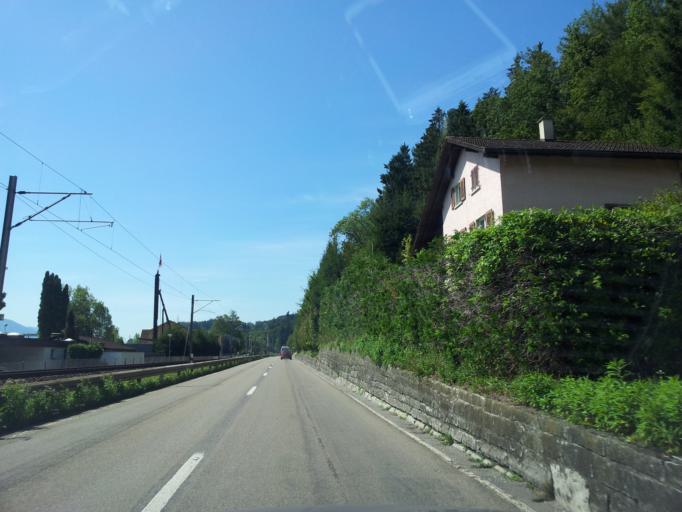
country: CH
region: Saint Gallen
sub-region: Wahlkreis See-Gaster
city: Eschenbach
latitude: 47.2261
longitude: 8.9280
